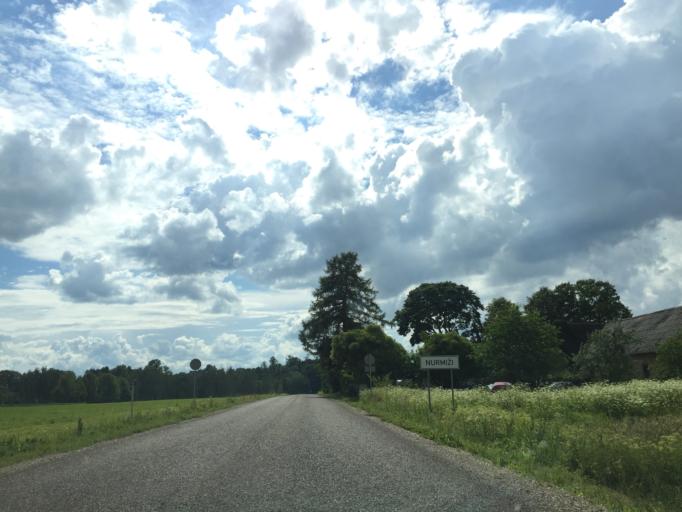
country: LV
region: Ligatne
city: Ligatne
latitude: 57.2022
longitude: 24.9537
